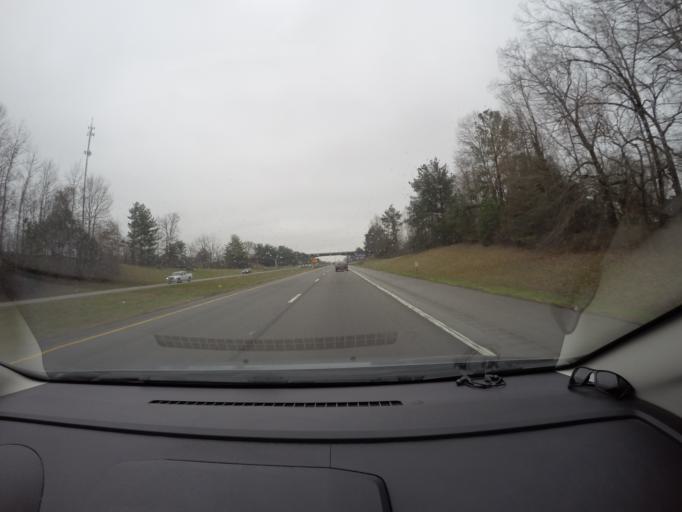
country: US
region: Tennessee
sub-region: Coffee County
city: Manchester
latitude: 35.4777
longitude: -86.0640
